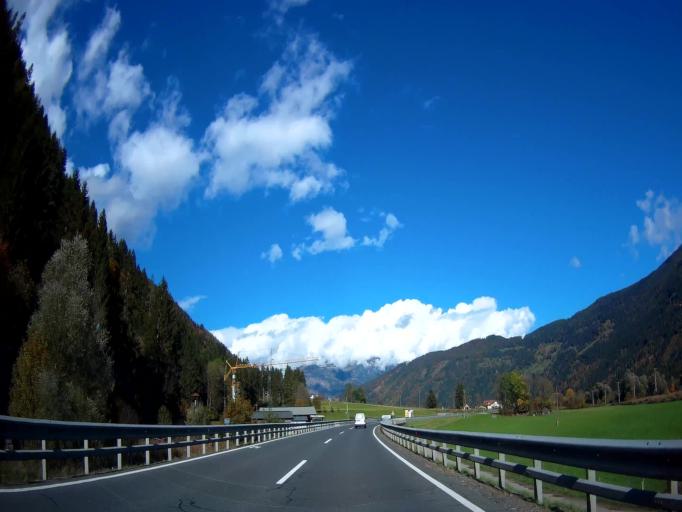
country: AT
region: Carinthia
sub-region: Politischer Bezirk Spittal an der Drau
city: Sachsenburg
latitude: 46.7791
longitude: 13.3447
